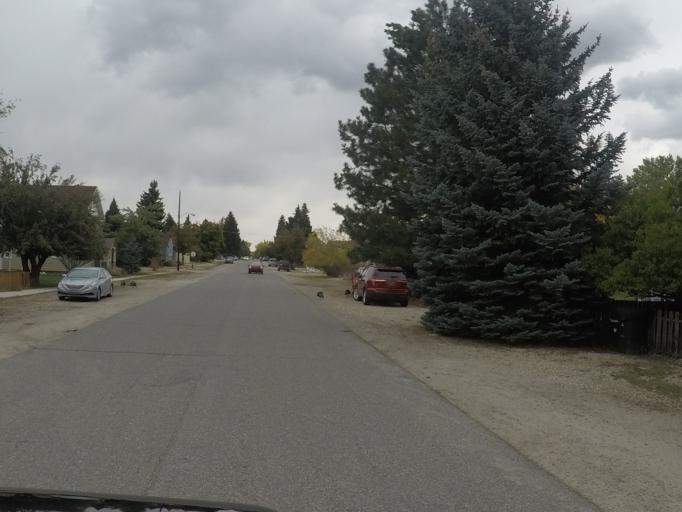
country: US
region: Montana
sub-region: Carbon County
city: Red Lodge
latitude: 45.1852
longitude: -109.2444
